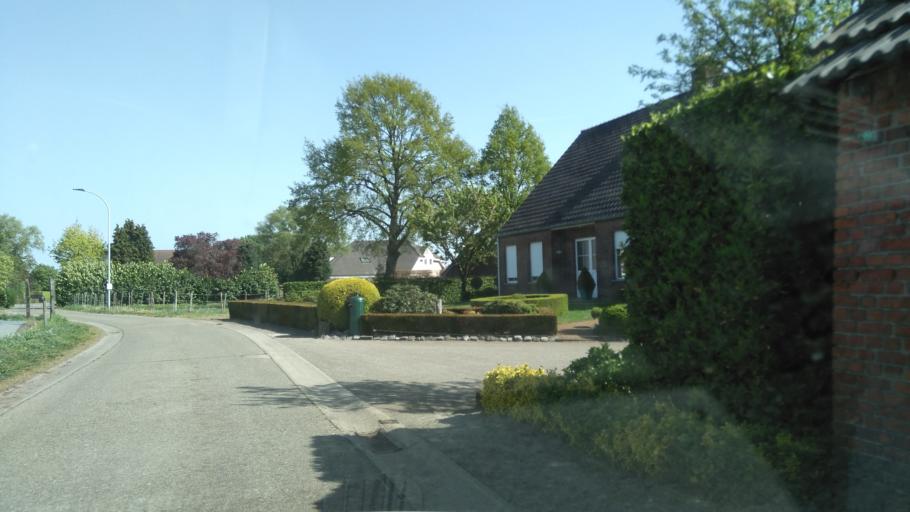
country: NL
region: North Brabant
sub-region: Gemeente Baarle-Nassau
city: Baarle-Nassau
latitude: 51.4332
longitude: 4.9355
